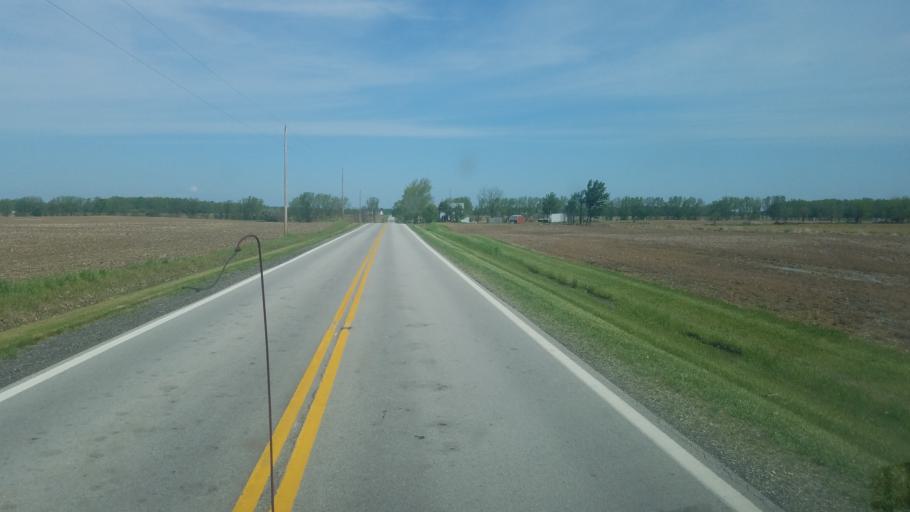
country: US
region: Ohio
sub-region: Seneca County
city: Tiffin
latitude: 40.9832
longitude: -83.0878
